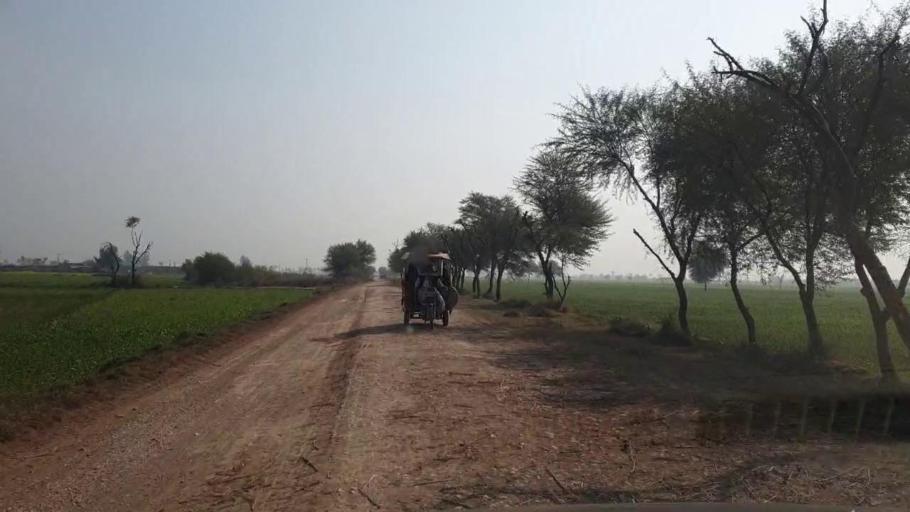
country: PK
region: Sindh
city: Hala
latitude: 25.9350
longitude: 68.4641
